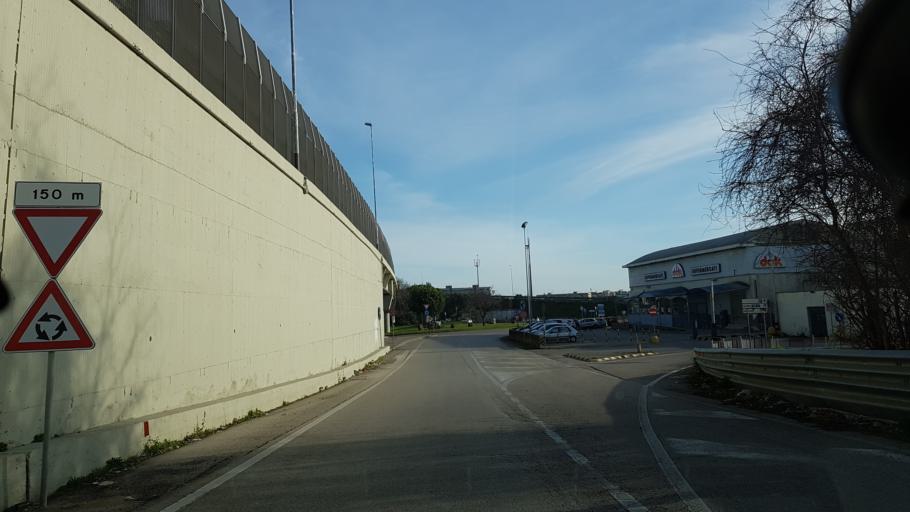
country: IT
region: Apulia
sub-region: Provincia di Brindisi
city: Brindisi
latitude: 40.6273
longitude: 17.9190
